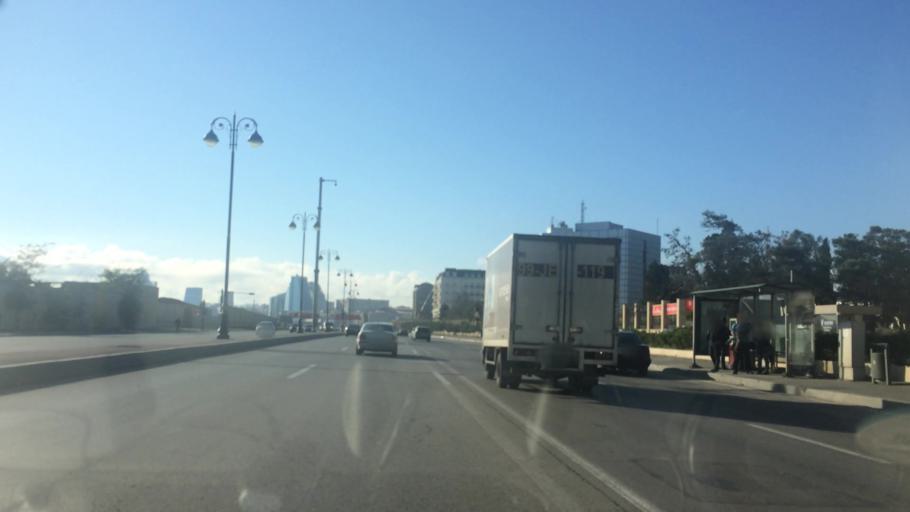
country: AZ
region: Baki
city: Baku
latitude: 40.3745
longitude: 49.8965
